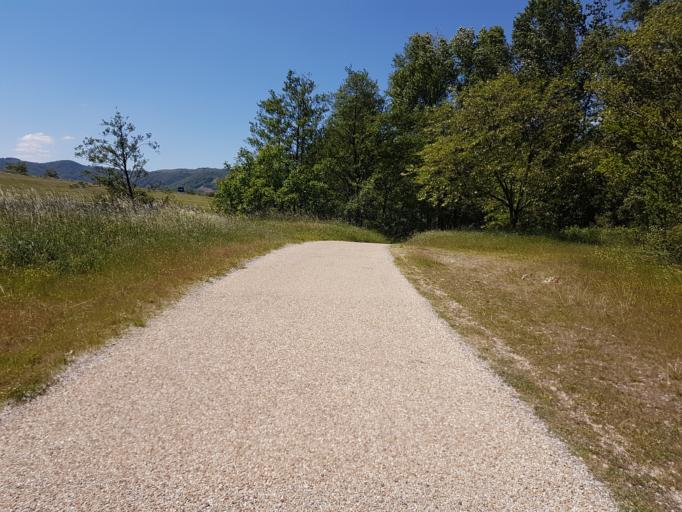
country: FR
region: Rhone-Alpes
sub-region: Departement de la Drome
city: Saint-Vallier
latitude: 45.1422
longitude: 4.8138
